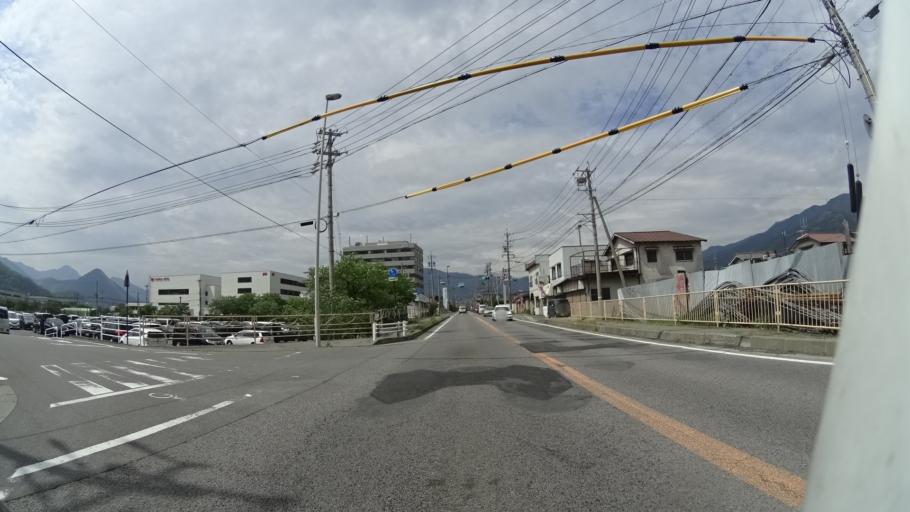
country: JP
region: Nagano
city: Ueda
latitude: 36.4340
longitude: 138.1921
